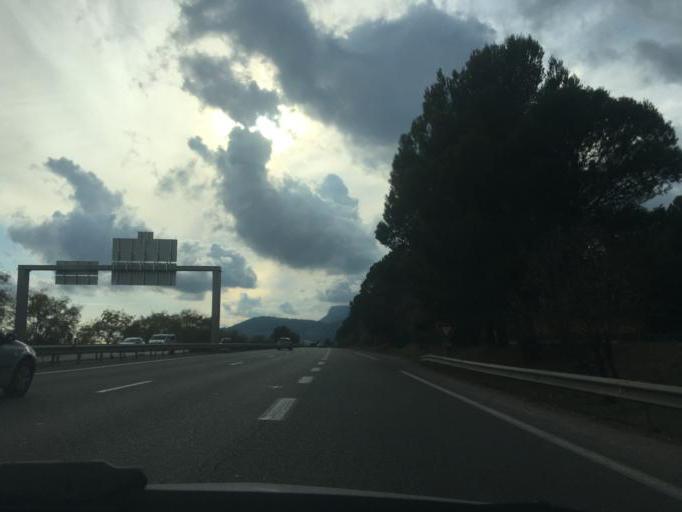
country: FR
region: Provence-Alpes-Cote d'Azur
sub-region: Departement du Var
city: Cuers
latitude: 43.2218
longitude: 6.0690
